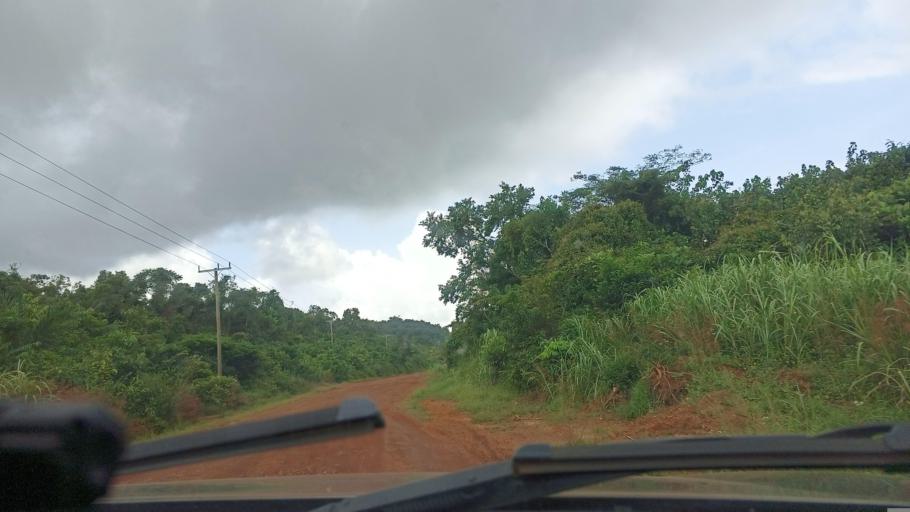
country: LR
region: Grand Cape Mount
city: Robertsport
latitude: 6.7096
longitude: -11.3349
